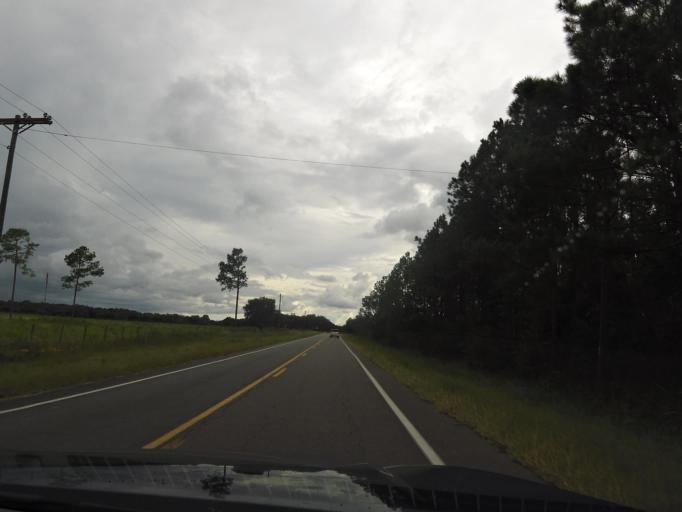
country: US
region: Florida
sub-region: Baker County
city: Macclenny
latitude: 30.4078
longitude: -82.1882
